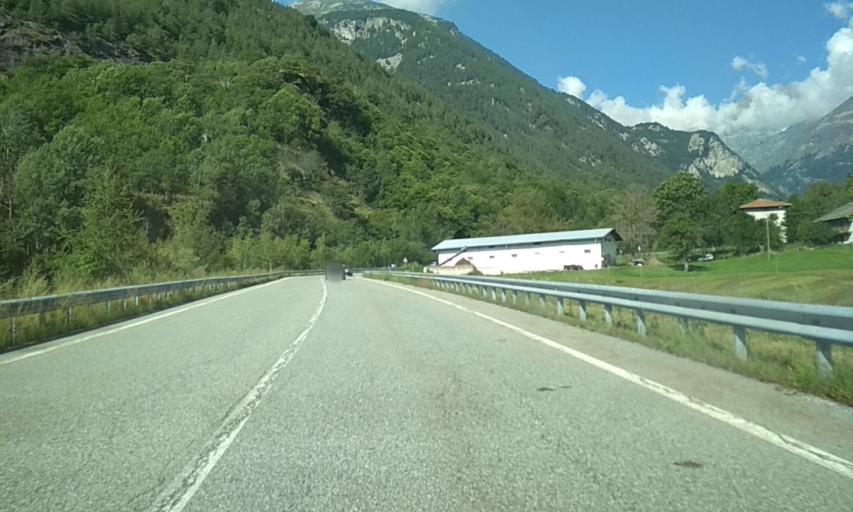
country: IT
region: Piedmont
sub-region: Provincia di Torino
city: Noasca
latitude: 45.4369
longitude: 7.3511
